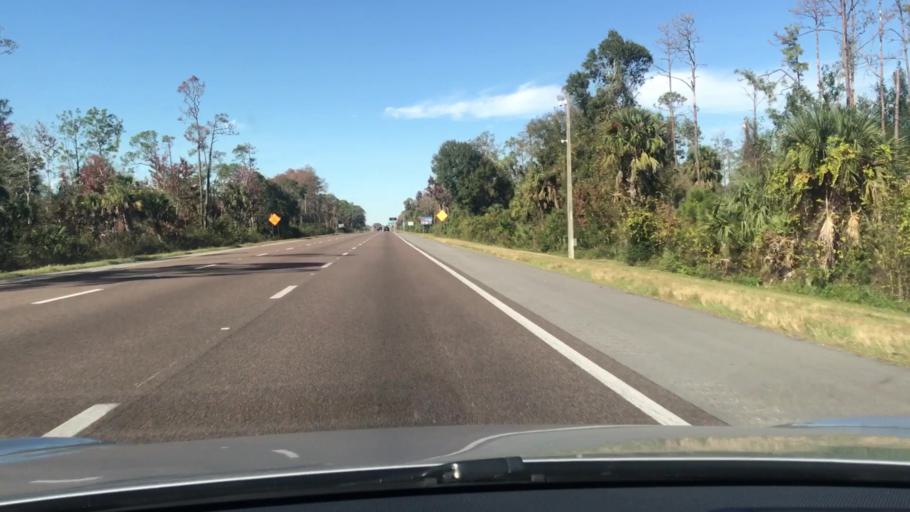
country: US
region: Florida
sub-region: Volusia County
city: Glencoe
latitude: 28.9997
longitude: -80.9790
